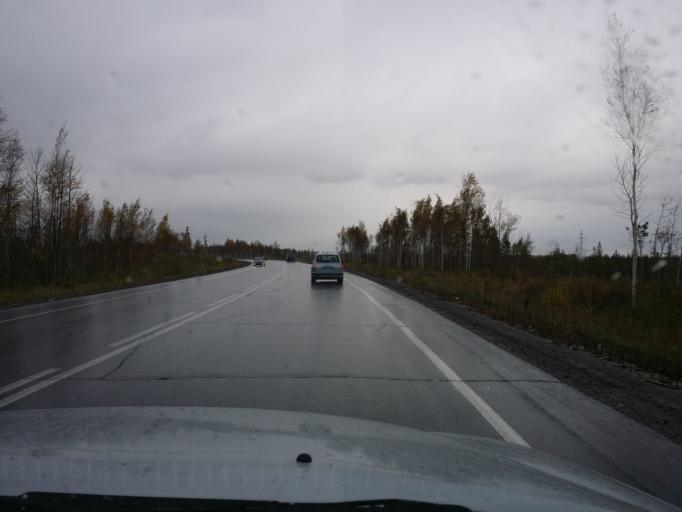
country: RU
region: Khanty-Mansiyskiy Avtonomnyy Okrug
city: Megion
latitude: 61.0686
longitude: 76.2489
